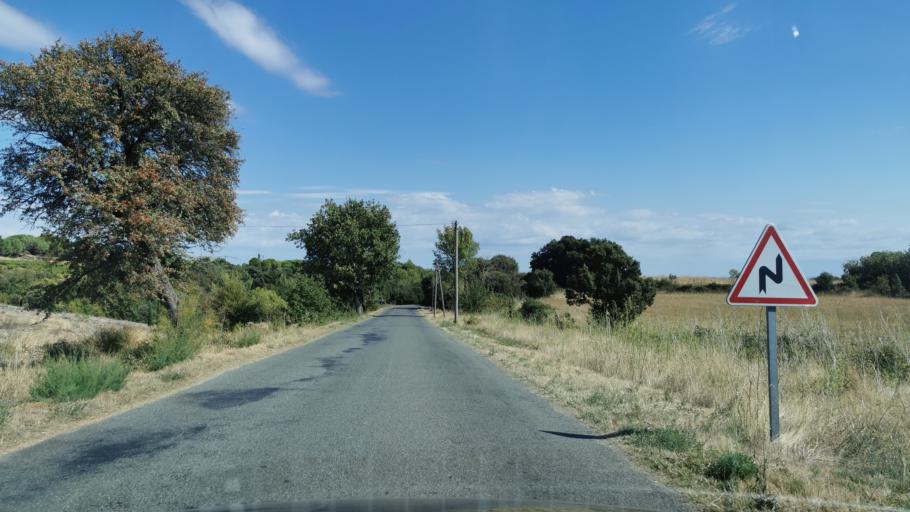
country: FR
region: Languedoc-Roussillon
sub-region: Departement de l'Aude
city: Caunes-Minervois
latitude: 43.3177
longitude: 2.5445
